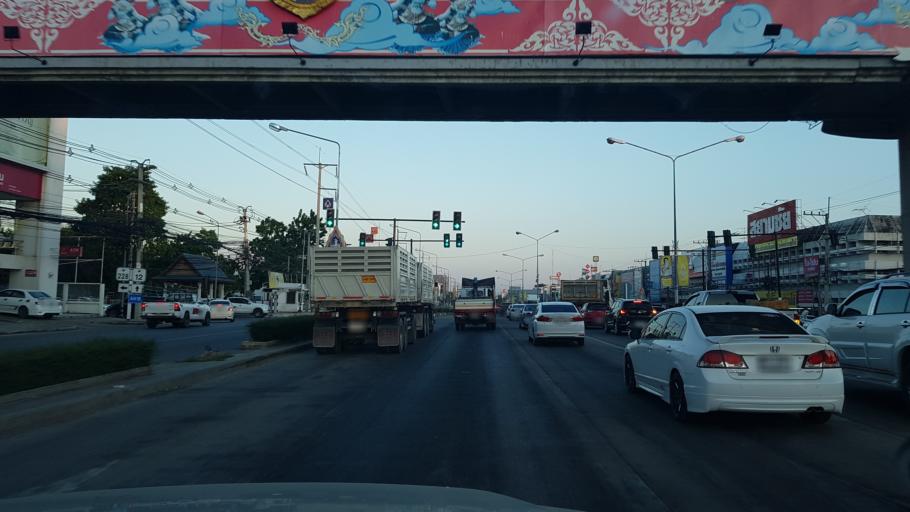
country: TH
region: Khon Kaen
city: Chum Phae
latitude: 16.5451
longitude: 102.0998
